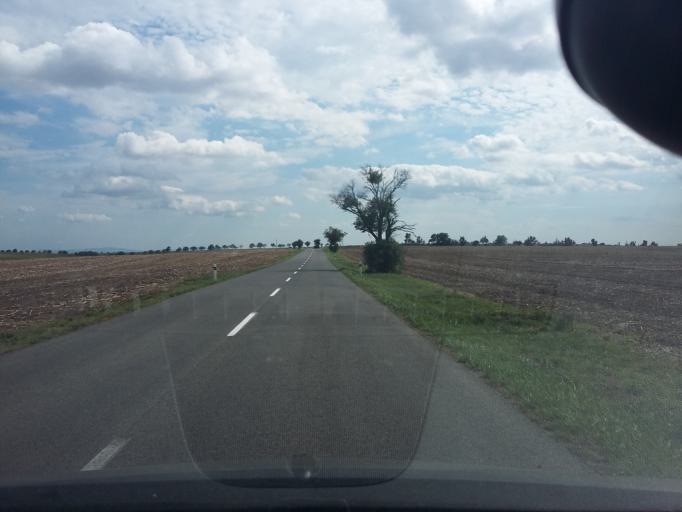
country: SK
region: Trnavsky
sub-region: Okres Skalica
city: Holic
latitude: 48.7694
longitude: 17.1737
